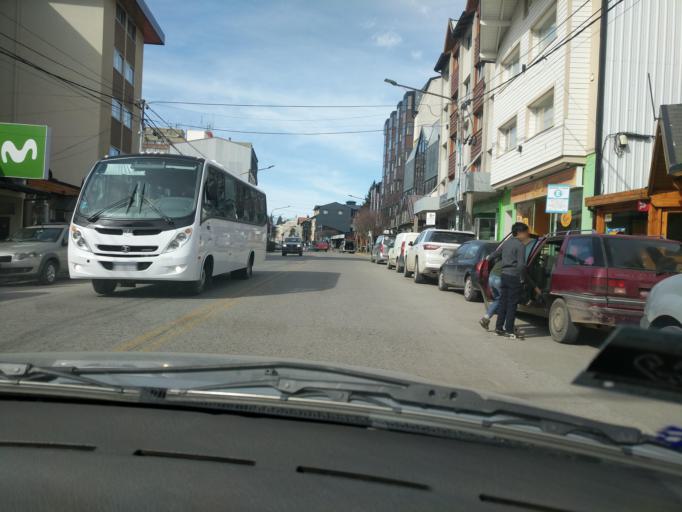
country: AR
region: Rio Negro
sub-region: Departamento de Bariloche
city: San Carlos de Bariloche
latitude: -41.1341
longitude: -71.3141
